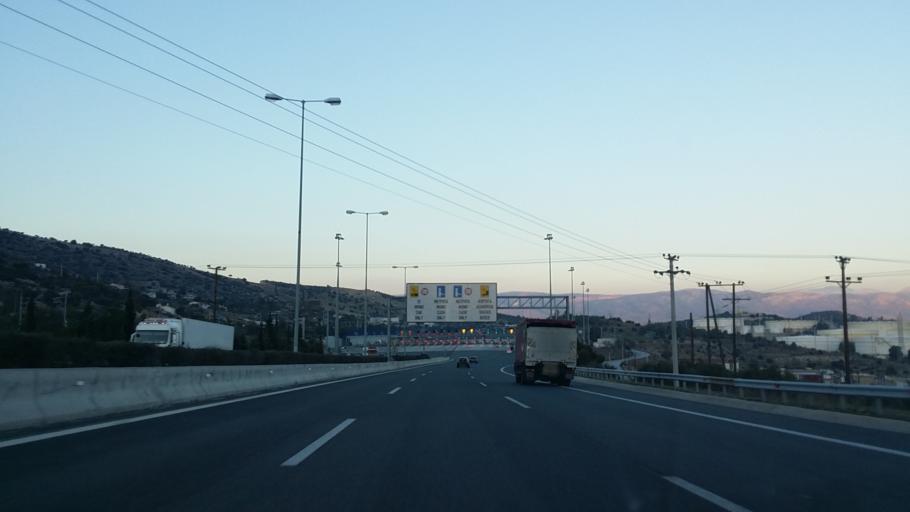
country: GR
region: Attica
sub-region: Nomarchia Dytikis Attikis
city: Mandra
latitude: 38.0378
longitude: 23.4927
